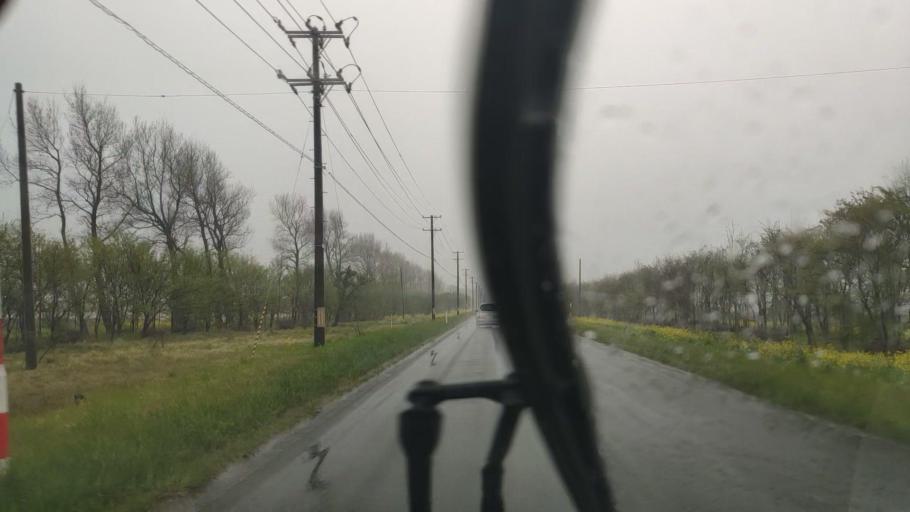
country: JP
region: Akita
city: Tenno
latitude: 39.9625
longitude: 139.9461
